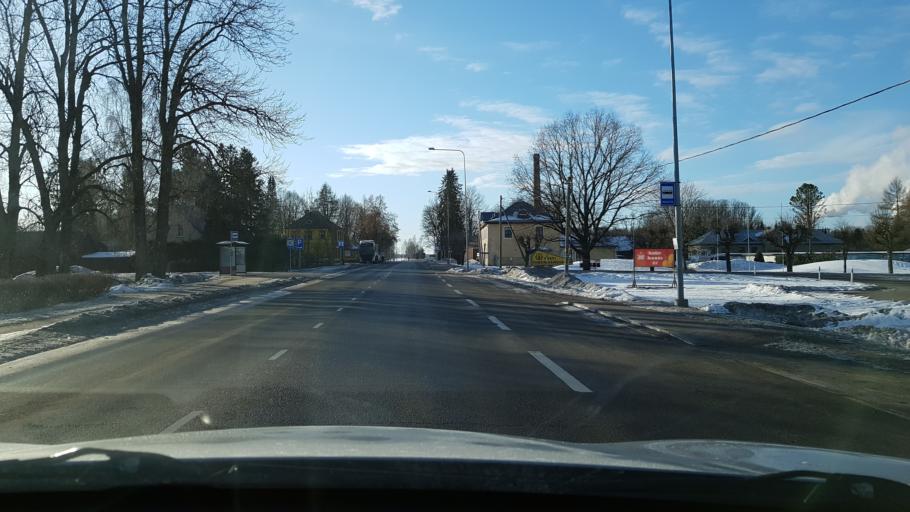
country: EE
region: Jogevamaa
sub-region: Poltsamaa linn
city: Poltsamaa
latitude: 58.7347
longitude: 25.7672
